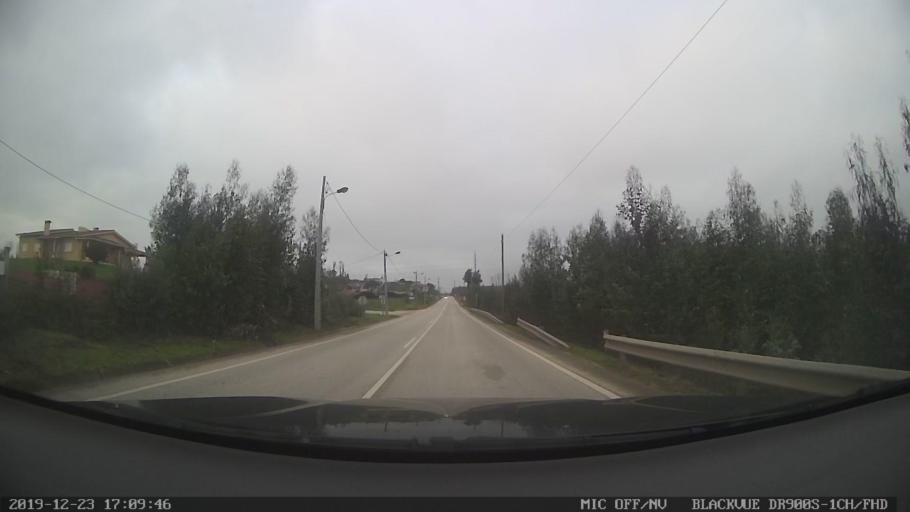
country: PT
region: Viseu
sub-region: Mortagua
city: Mortagua
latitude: 40.3740
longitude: -8.1947
